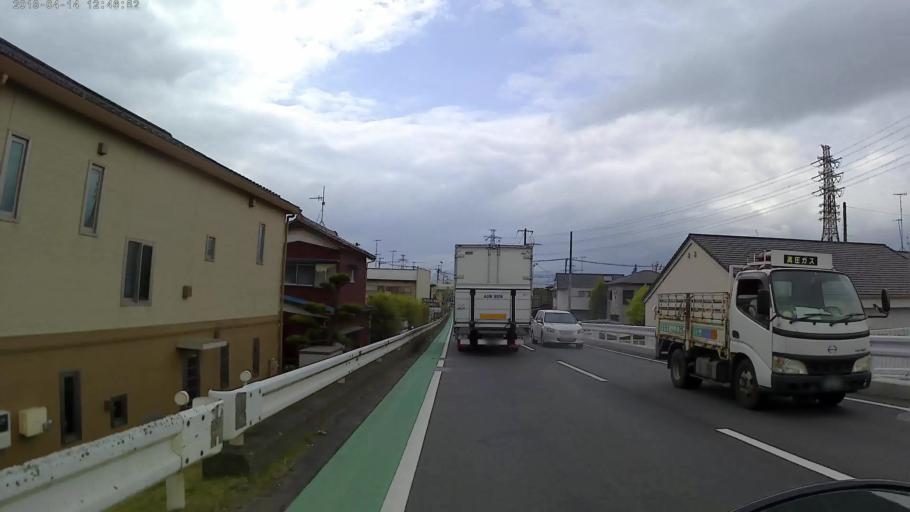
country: JP
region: Kanagawa
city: Atsugi
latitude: 35.4050
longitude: 139.3671
